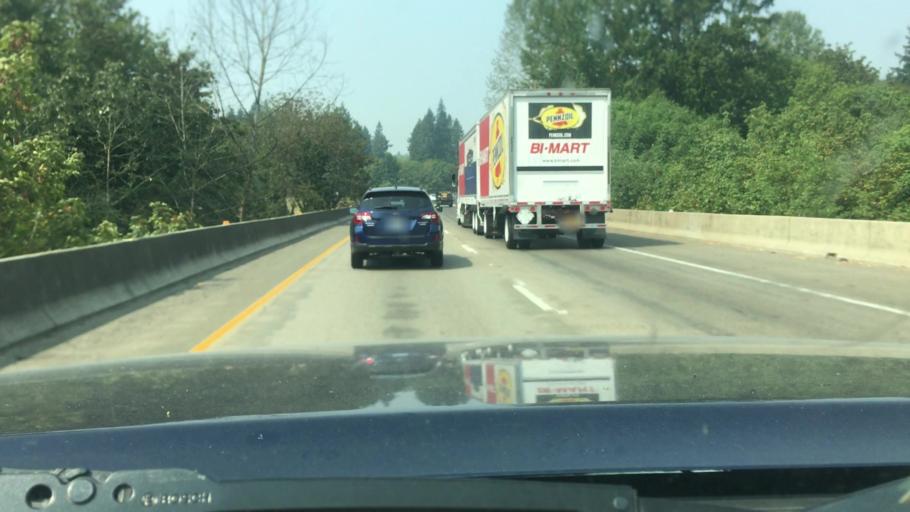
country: US
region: Oregon
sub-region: Clackamas County
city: Stafford
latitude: 45.3668
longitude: -122.6885
